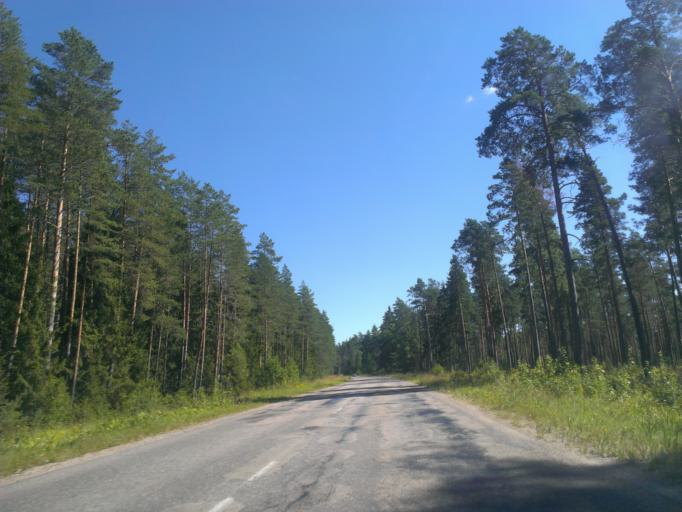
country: LV
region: Incukalns
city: Incukalns
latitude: 57.0305
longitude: 24.7117
